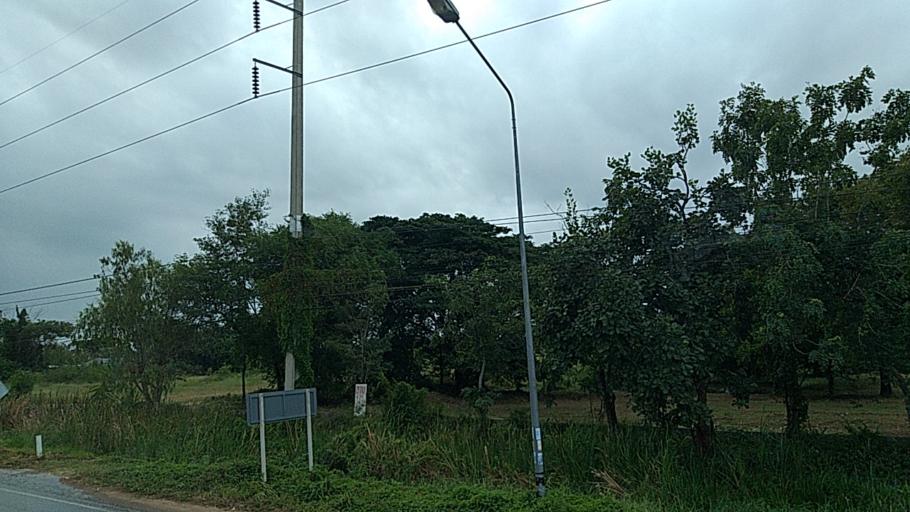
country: TH
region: Maha Sarakham
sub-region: Amphoe Borabue
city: Borabue
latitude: 16.0425
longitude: 103.1267
